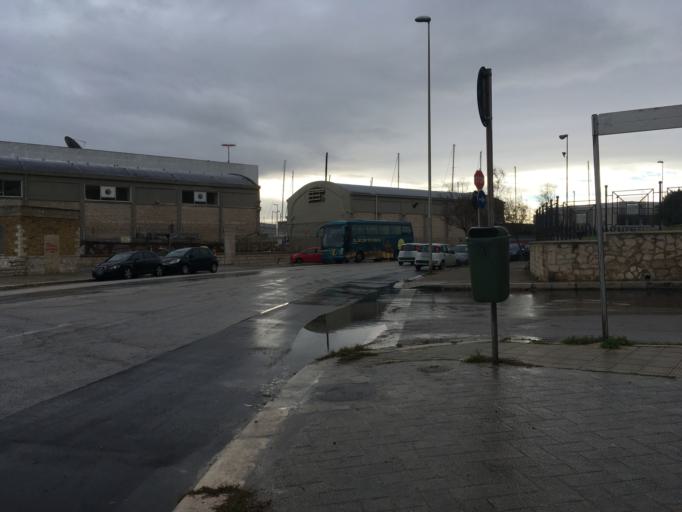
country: IT
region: Apulia
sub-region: Provincia di Bari
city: Bari
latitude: 41.1383
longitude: 16.8465
